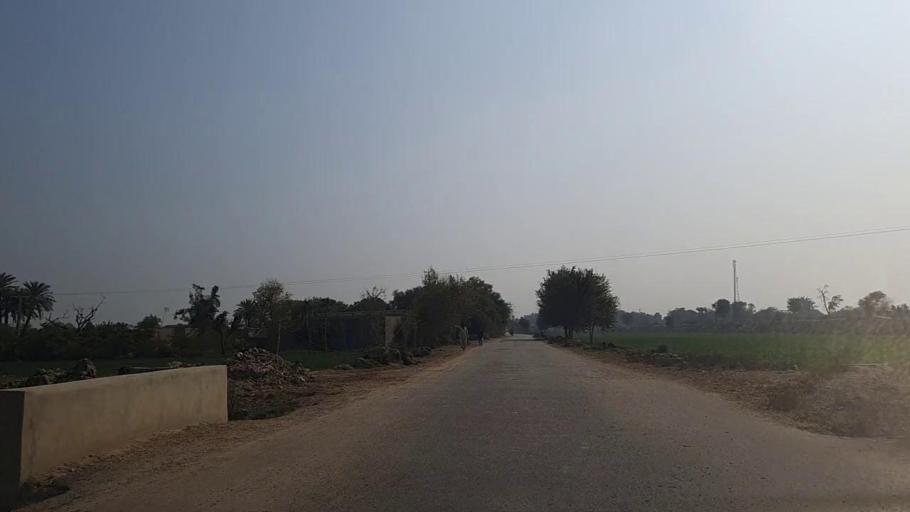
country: PK
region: Sindh
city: Jam Sahib
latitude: 26.3364
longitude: 68.5355
